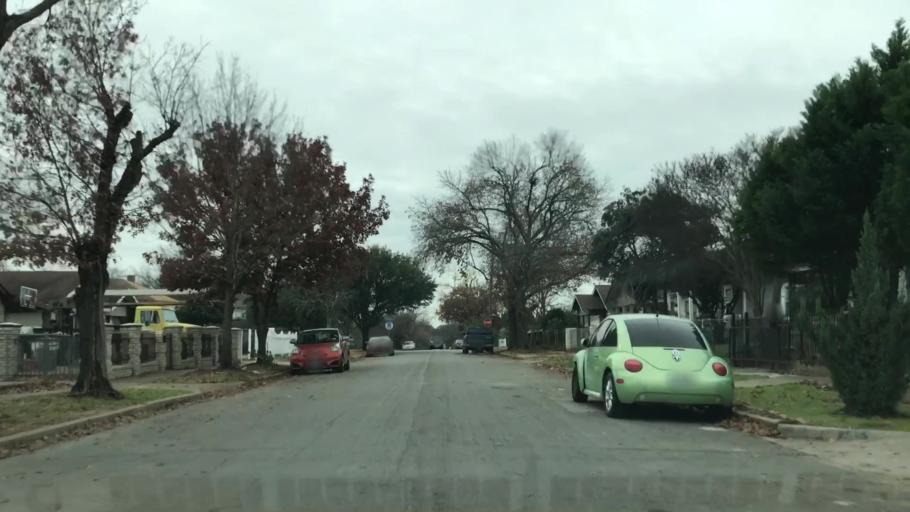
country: US
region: Texas
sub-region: Dallas County
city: Cockrell Hill
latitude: 32.7402
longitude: -96.8491
